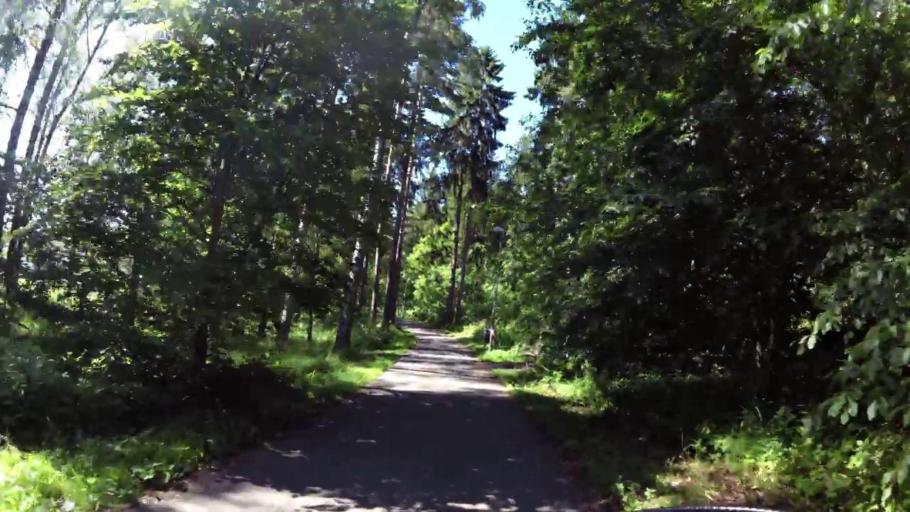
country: SE
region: OEstergoetland
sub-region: Linkopings Kommun
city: Linkoping
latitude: 58.3991
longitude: 15.6337
